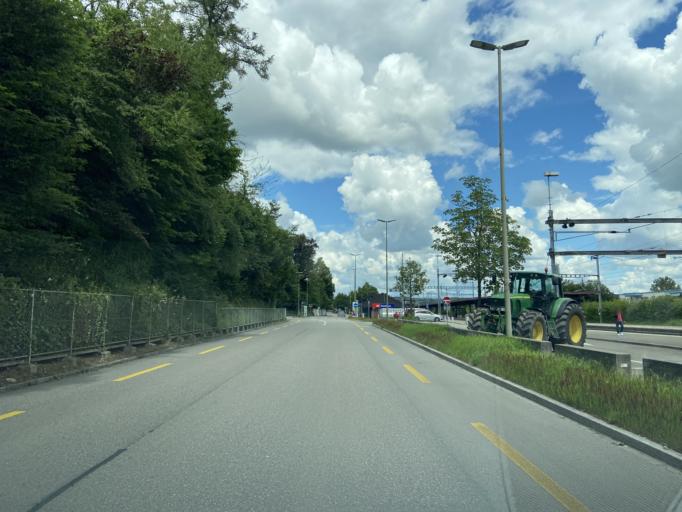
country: CH
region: Zurich
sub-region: Bezirk Buelach
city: Dietlikon / Dietlikon (Dorf)
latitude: 47.4190
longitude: 8.6185
